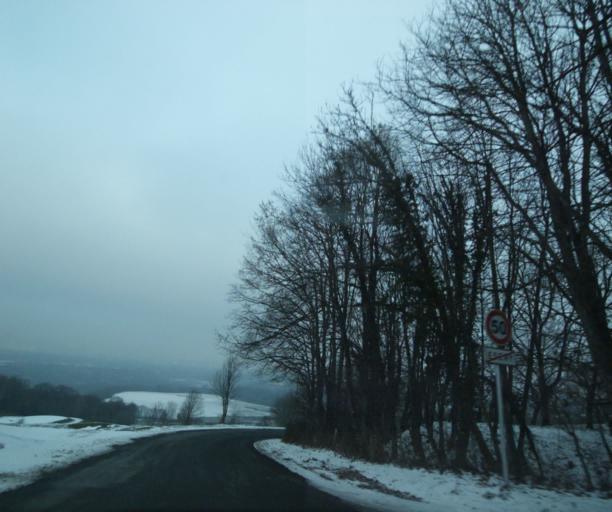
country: FR
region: Rhone-Alpes
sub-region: Departement de la Haute-Savoie
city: Reignier-Esery
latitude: 46.1444
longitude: 6.2397
